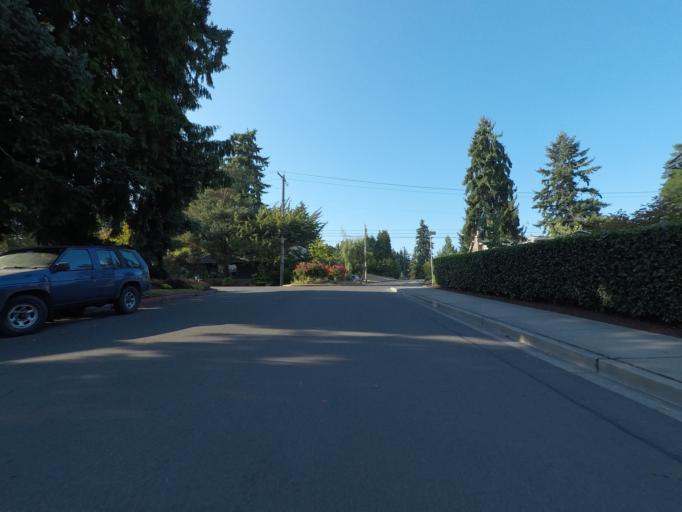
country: US
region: Washington
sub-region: King County
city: Kirkland
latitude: 47.6828
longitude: -122.2017
